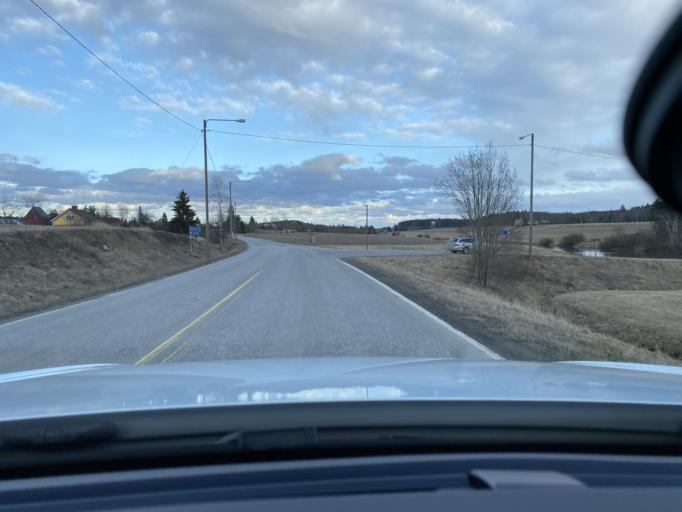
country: FI
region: Pirkanmaa
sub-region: Lounais-Pirkanmaa
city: Punkalaidun
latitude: 61.1217
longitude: 23.0505
